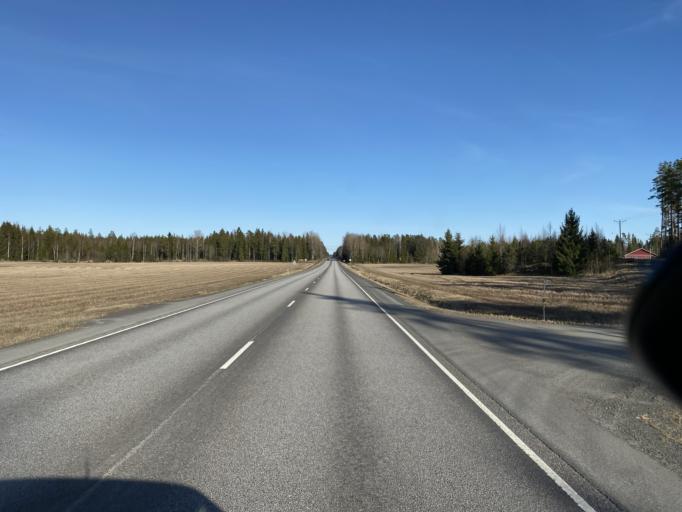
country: FI
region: Satakunta
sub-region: Rauma
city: Eura
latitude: 61.1312
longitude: 22.0429
